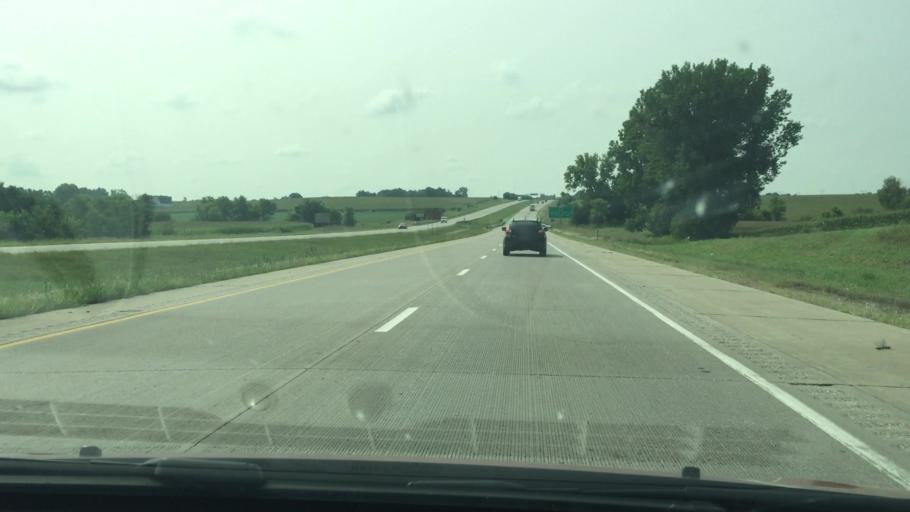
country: US
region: Iowa
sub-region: Scott County
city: Walcott
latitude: 41.5583
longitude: -90.6786
